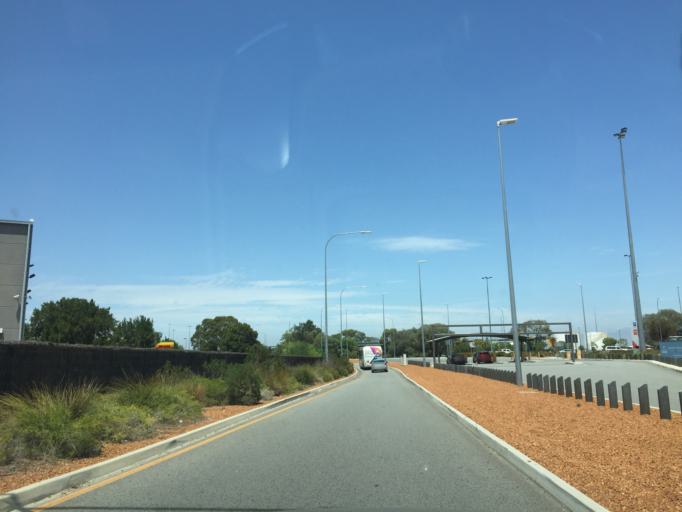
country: AU
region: Western Australia
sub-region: Belmont
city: Redcliffe
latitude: -31.9449
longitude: 115.9755
